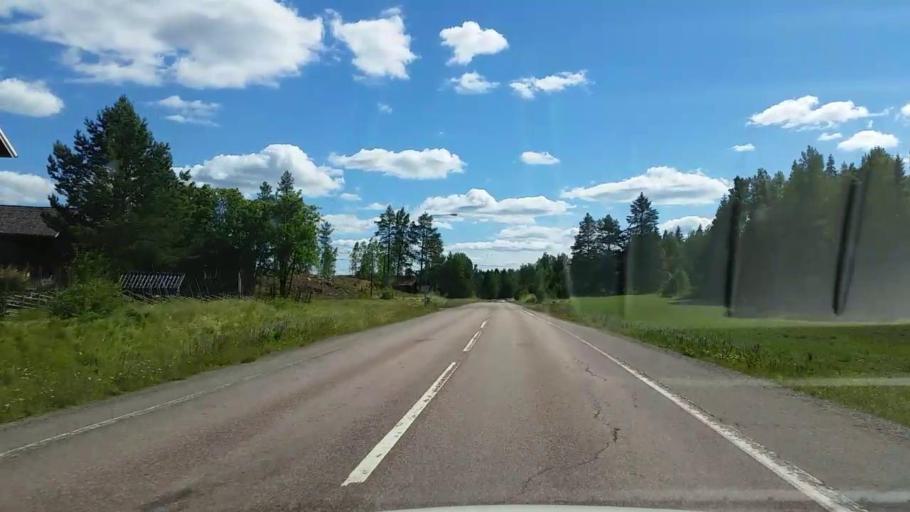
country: SE
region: Dalarna
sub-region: Faluns Kommun
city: Svardsjo
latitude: 60.8360
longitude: 15.7602
